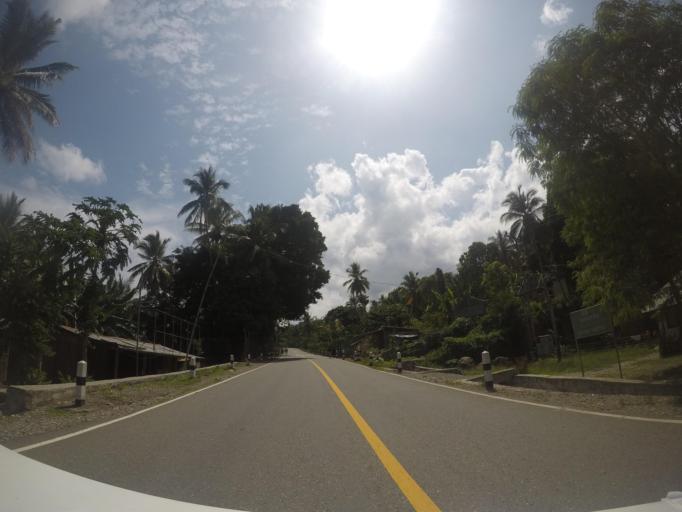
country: TL
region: Baucau
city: Baucau
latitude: -8.4879
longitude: 126.3364
